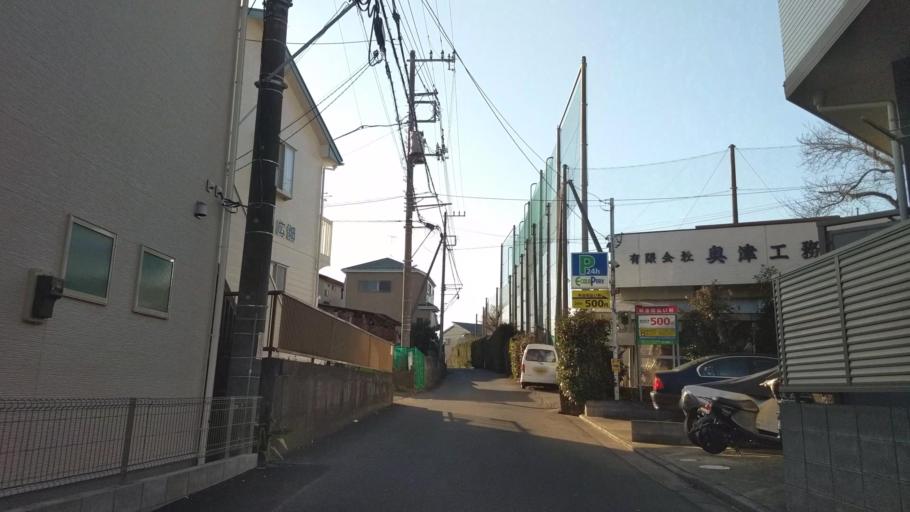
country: JP
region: Kanagawa
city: Hadano
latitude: 35.3619
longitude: 139.2604
